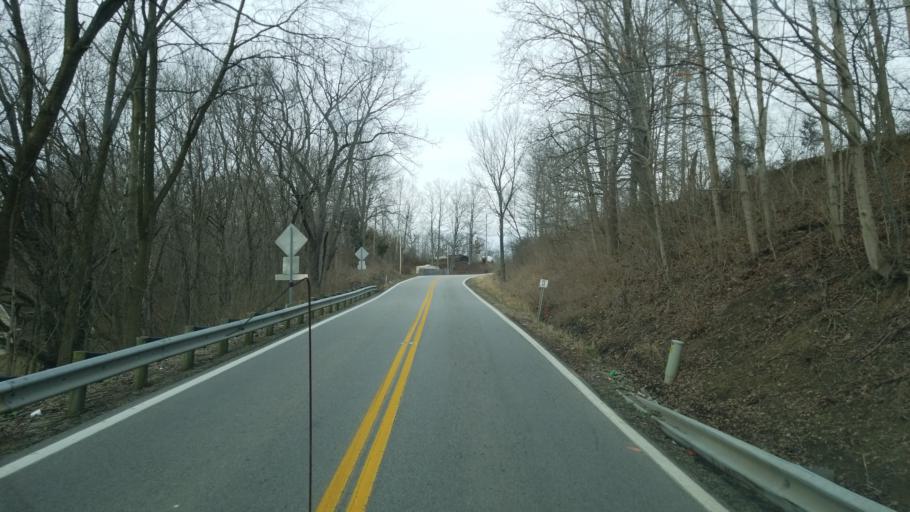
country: US
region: Ohio
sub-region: Ross County
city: Frankfort
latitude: 39.4376
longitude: -83.2222
